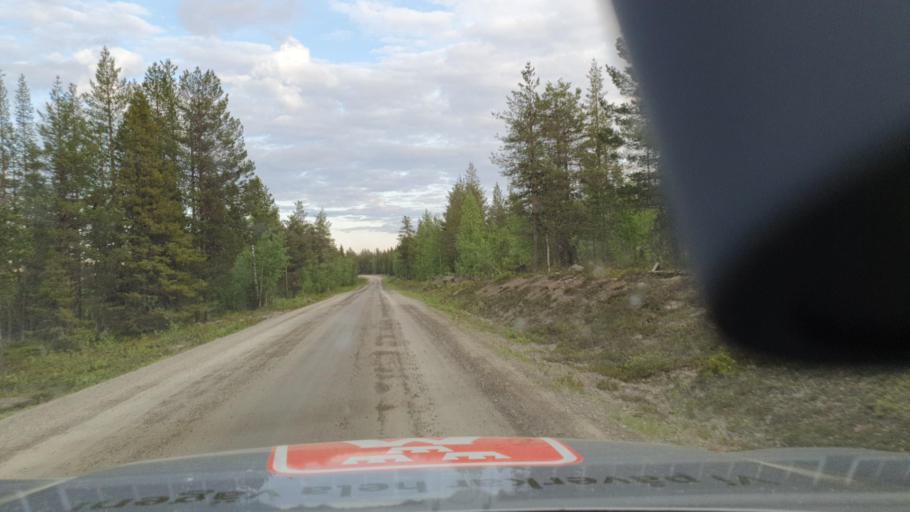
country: SE
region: Norrbotten
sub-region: Gallivare Kommun
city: Gaellivare
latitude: 66.7097
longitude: 21.1534
